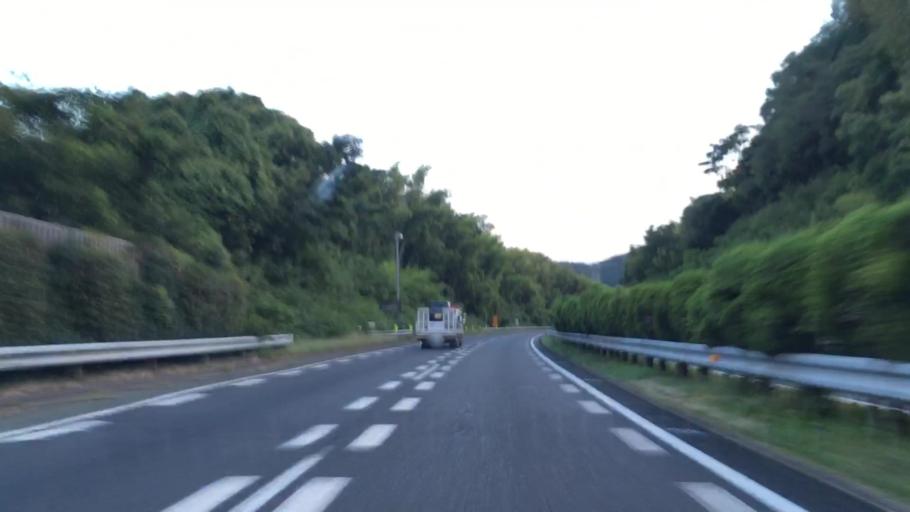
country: JP
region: Yamaguchi
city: Shimonoseki
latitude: 33.9355
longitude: 130.9962
